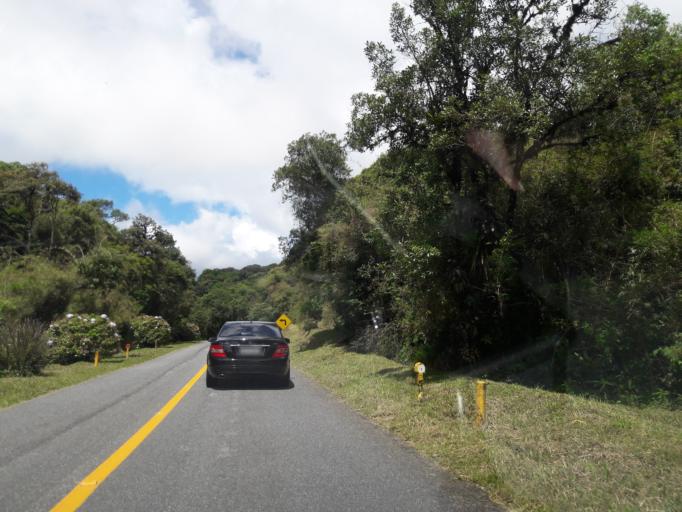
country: BR
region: Parana
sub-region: Campina Grande Do Sul
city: Campina Grande do Sul
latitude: -25.3326
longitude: -48.9022
